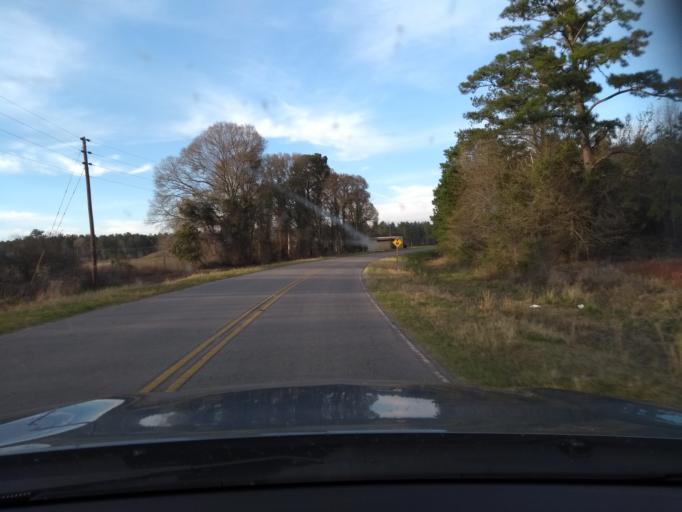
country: US
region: Georgia
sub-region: Bulloch County
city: Brooklet
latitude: 32.2859
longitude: -81.7583
